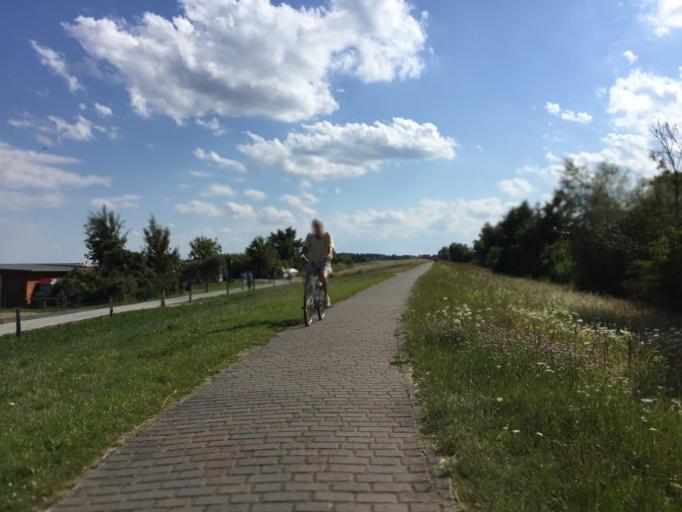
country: DE
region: Mecklenburg-Vorpommern
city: Hiddensee
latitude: 54.5843
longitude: 13.1103
